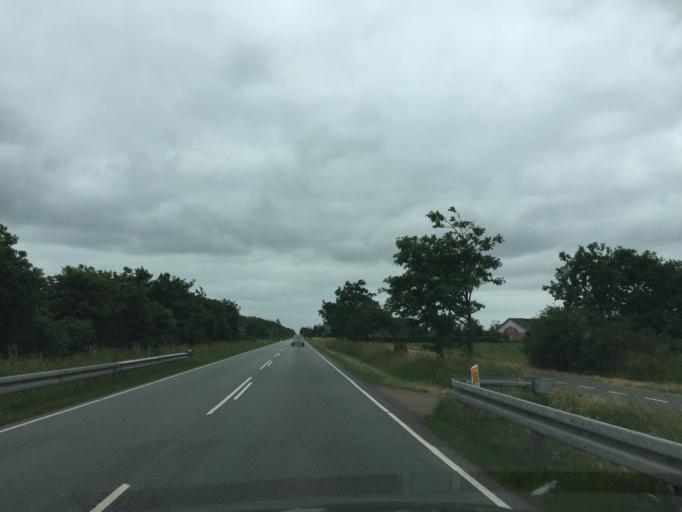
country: DK
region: South Denmark
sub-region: Esbjerg Kommune
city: Ribe
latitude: 55.3121
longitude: 8.7494
